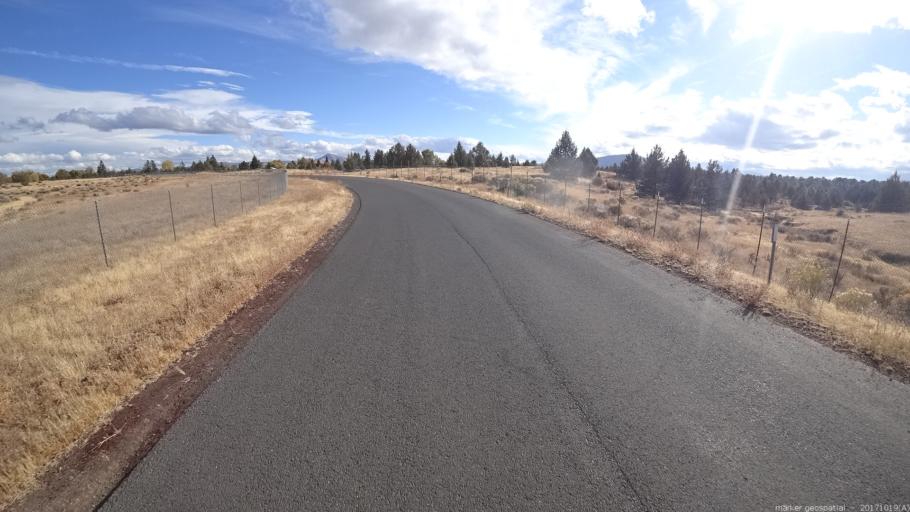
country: US
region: California
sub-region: Shasta County
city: Burney
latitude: 41.0109
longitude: -121.4419
